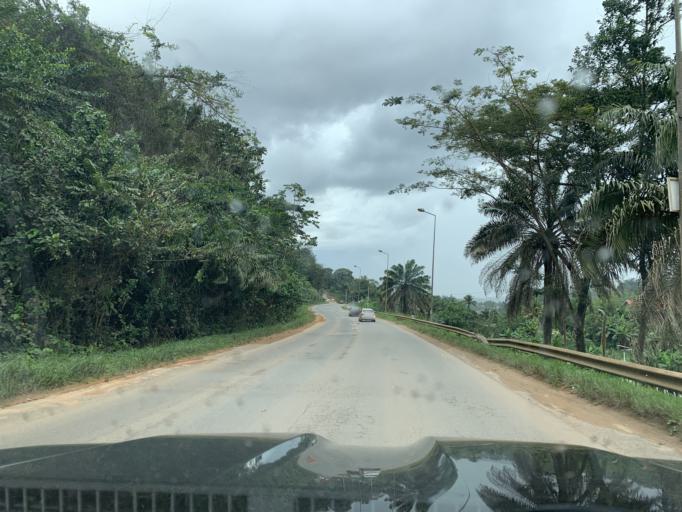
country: GH
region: Western
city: Tarkwa
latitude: 5.3208
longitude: -1.9861
